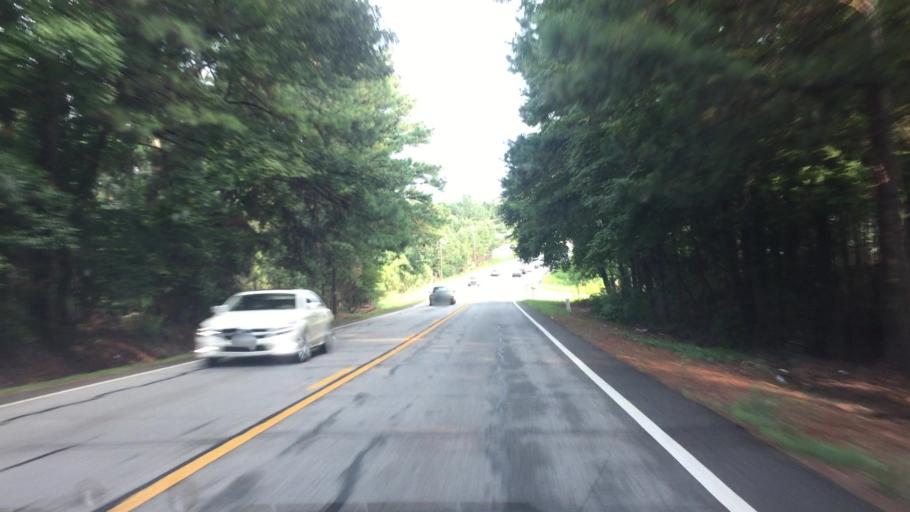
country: US
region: Georgia
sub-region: Henry County
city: Stockbridge
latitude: 33.5884
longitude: -84.1504
